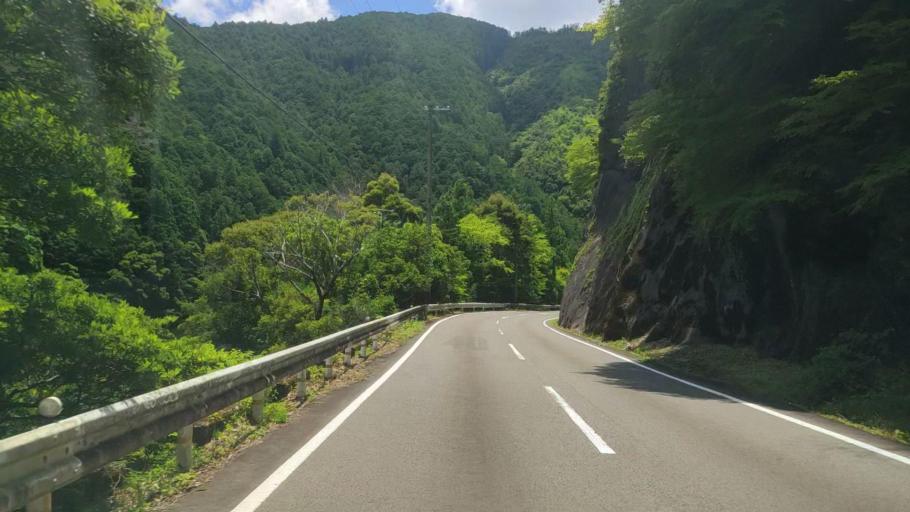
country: JP
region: Mie
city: Owase
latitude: 33.9968
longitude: 136.0144
